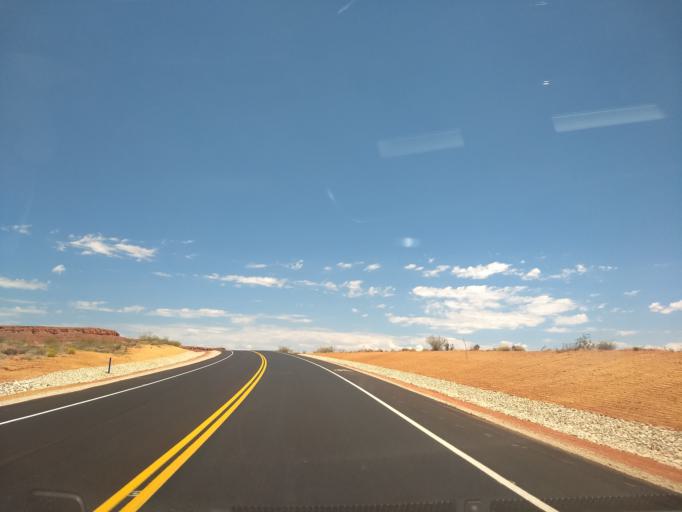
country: US
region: Utah
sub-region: Washington County
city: Washington
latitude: 37.1484
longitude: -113.5029
